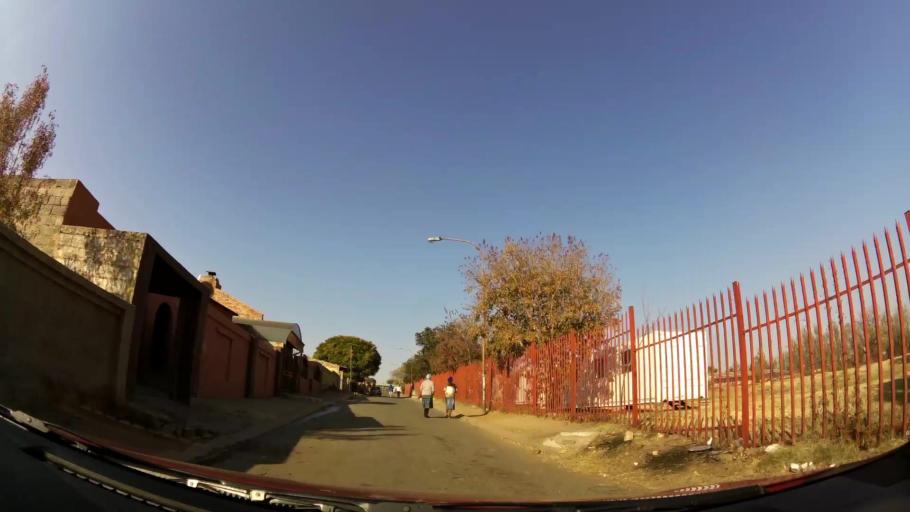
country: ZA
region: Gauteng
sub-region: City of Johannesburg Metropolitan Municipality
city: Soweto
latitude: -26.2579
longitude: 27.9466
